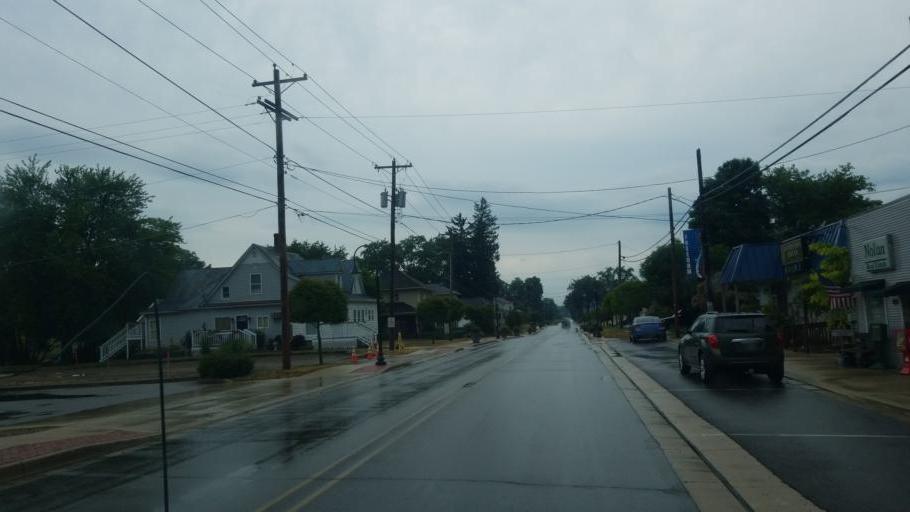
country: US
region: Indiana
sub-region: Steuben County
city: Hamilton
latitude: 41.5335
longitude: -84.9132
